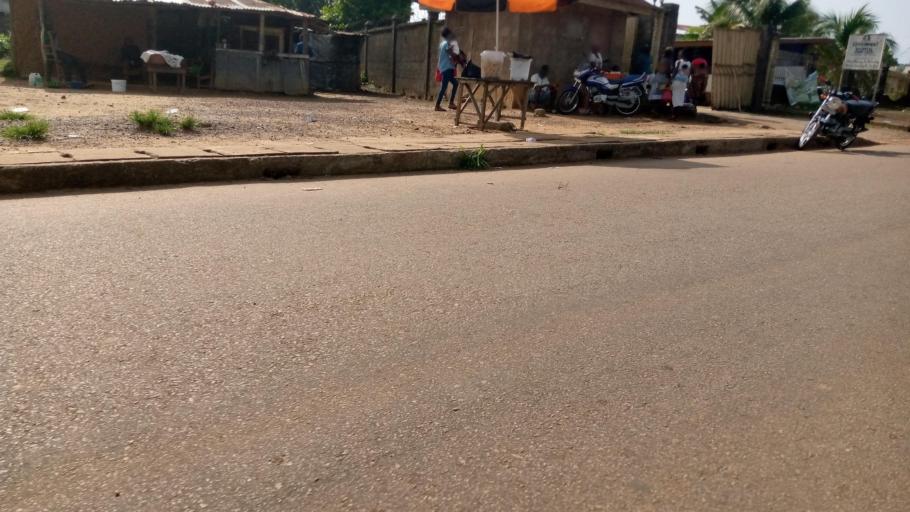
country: SL
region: Southern Province
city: Pujehun
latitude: 7.3537
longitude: -11.7207
